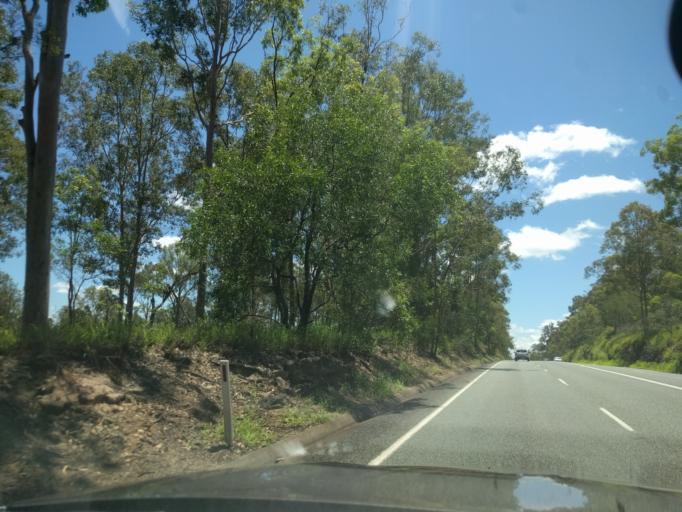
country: AU
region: Queensland
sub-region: Logan
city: Cedar Vale
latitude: -27.8540
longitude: 153.0109
